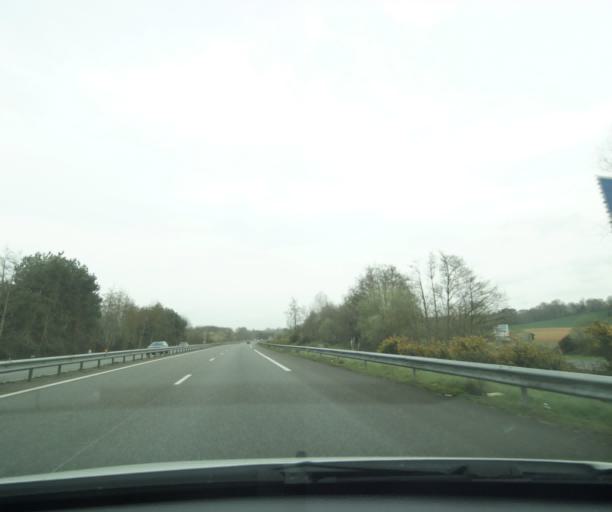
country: FR
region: Aquitaine
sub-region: Departement des Pyrenees-Atlantiques
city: Bidache
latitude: 43.5315
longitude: -1.1703
